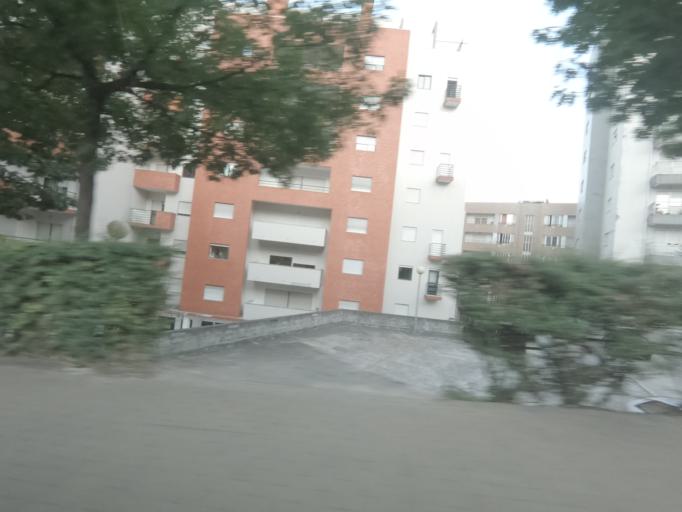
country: PT
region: Vila Real
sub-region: Vila Real
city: Vila Real
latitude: 41.3038
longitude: -7.7396
